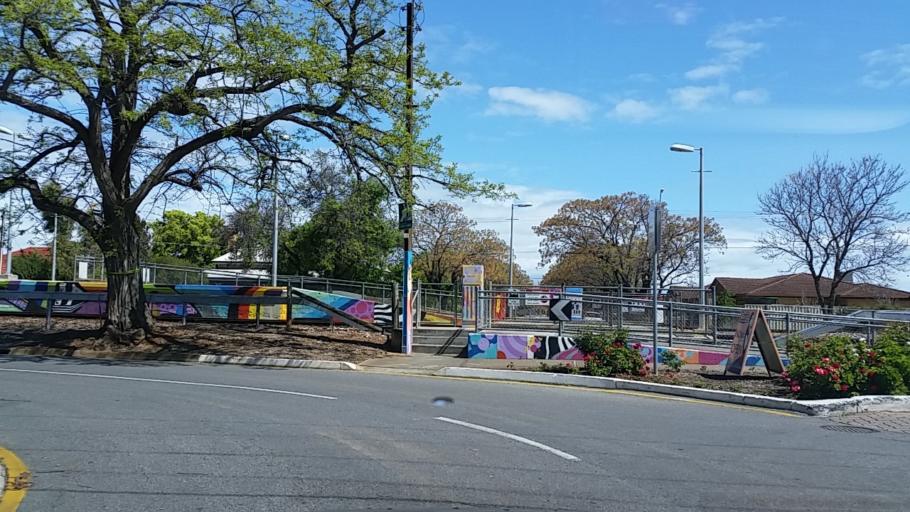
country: AU
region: South Australia
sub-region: Charles Sturt
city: Woodville
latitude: -34.8808
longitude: 138.5432
